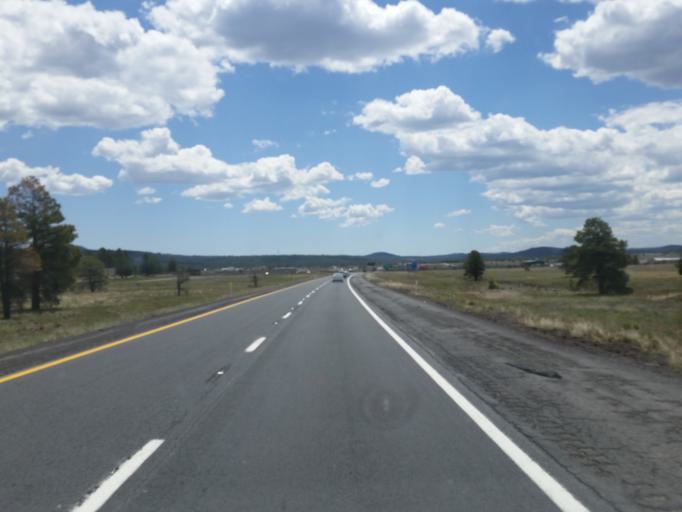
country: US
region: Arizona
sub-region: Coconino County
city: Parks
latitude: 35.2440
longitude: -111.8400
